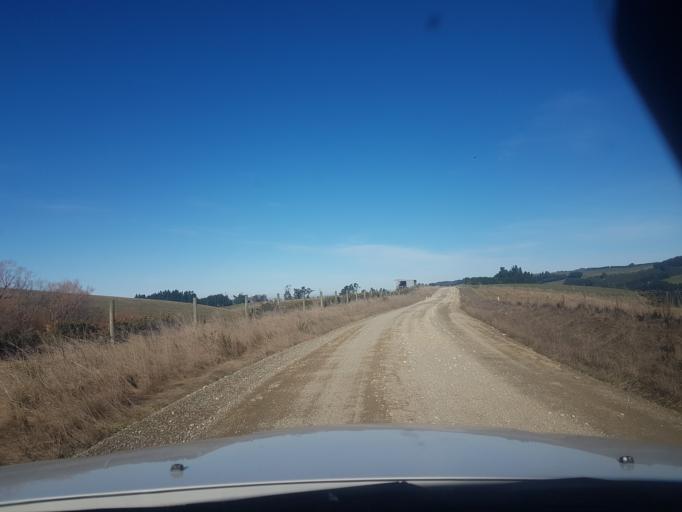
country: NZ
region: Canterbury
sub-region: Timaru District
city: Pleasant Point
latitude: -44.3658
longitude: 171.0719
